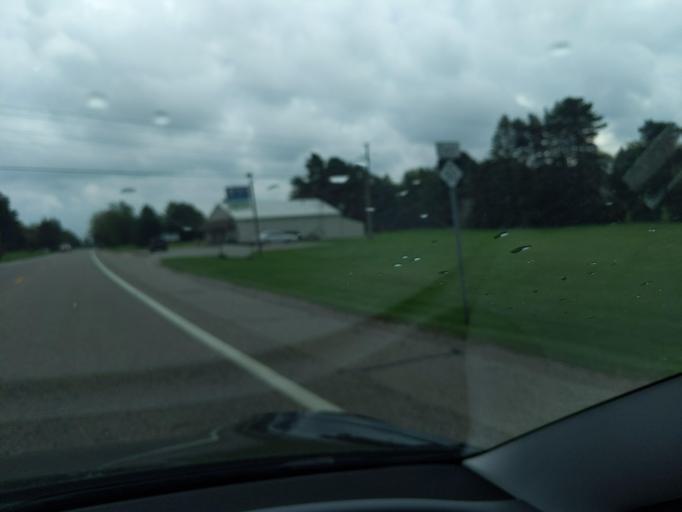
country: US
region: Michigan
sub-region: Eaton County
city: Charlotte
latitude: 42.5521
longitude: -84.7581
